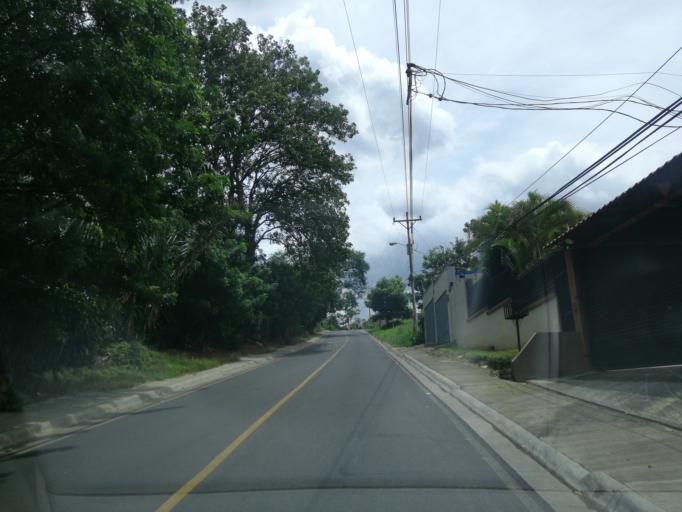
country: CR
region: Alajuela
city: Alajuela
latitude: 10.0235
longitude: -84.1971
